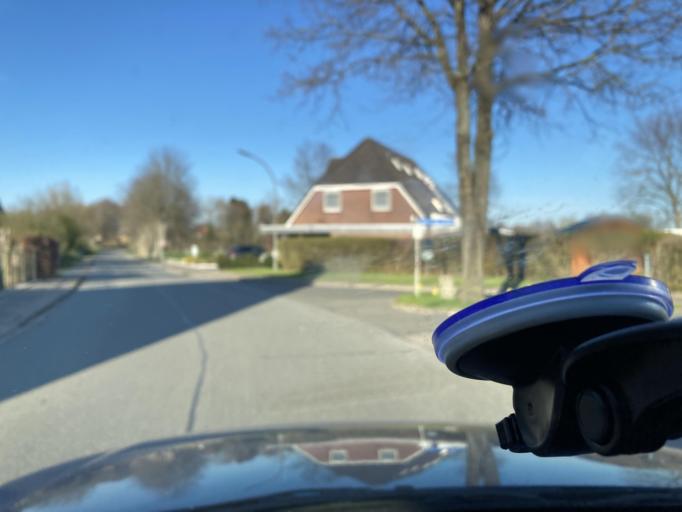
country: DE
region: Schleswig-Holstein
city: Wesseln
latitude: 54.2090
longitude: 9.0800
